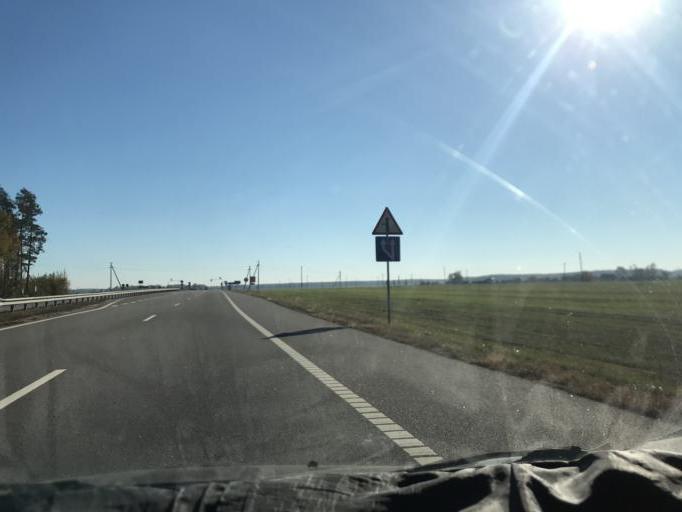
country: BY
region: Mogilev
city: Yalizava
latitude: 53.2237
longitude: 29.0122
